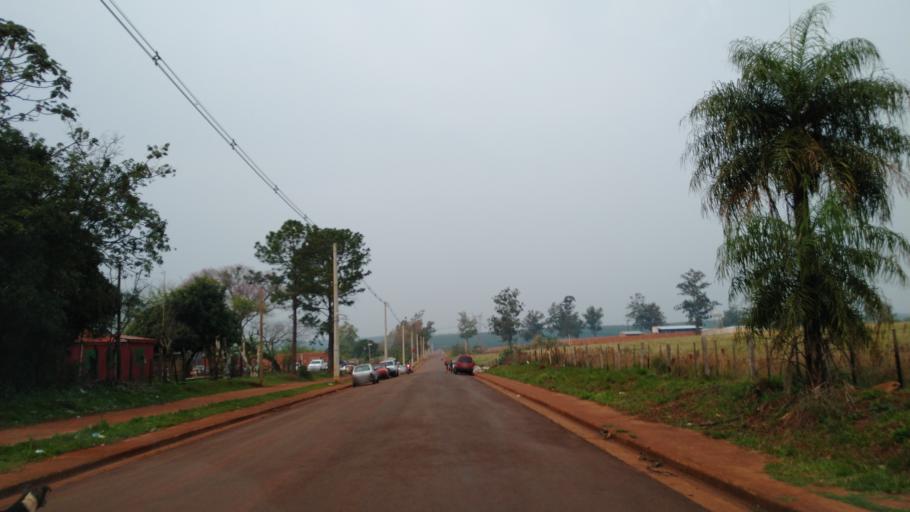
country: AR
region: Misiones
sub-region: Departamento de Capital
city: Posadas
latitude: -27.4450
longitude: -55.9332
